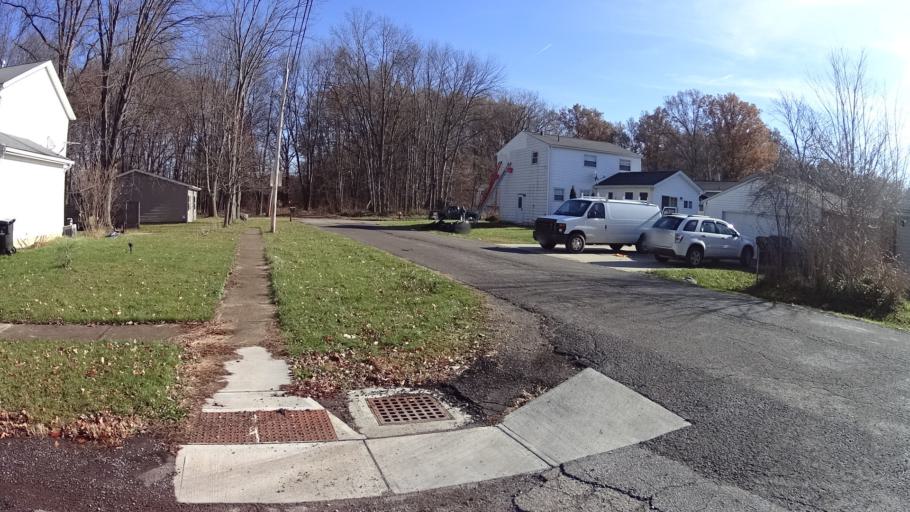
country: US
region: Ohio
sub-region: Lorain County
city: North Ridgeville
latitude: 41.4134
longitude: -81.9864
